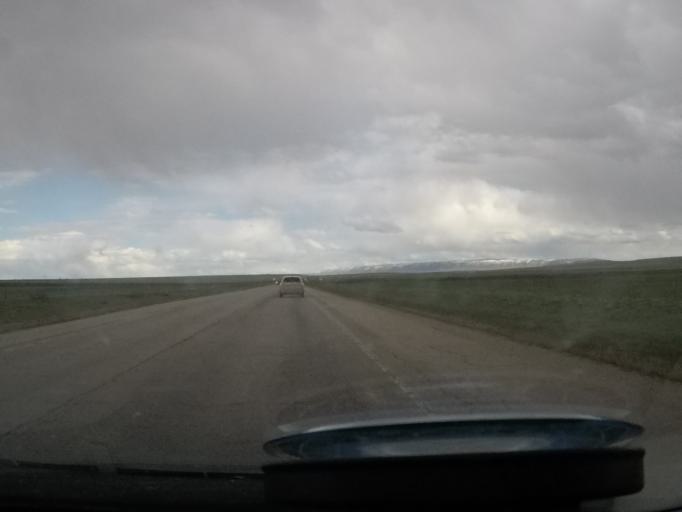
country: US
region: Wyoming
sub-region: Natrona County
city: Mills
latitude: 42.9522
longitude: -106.6382
